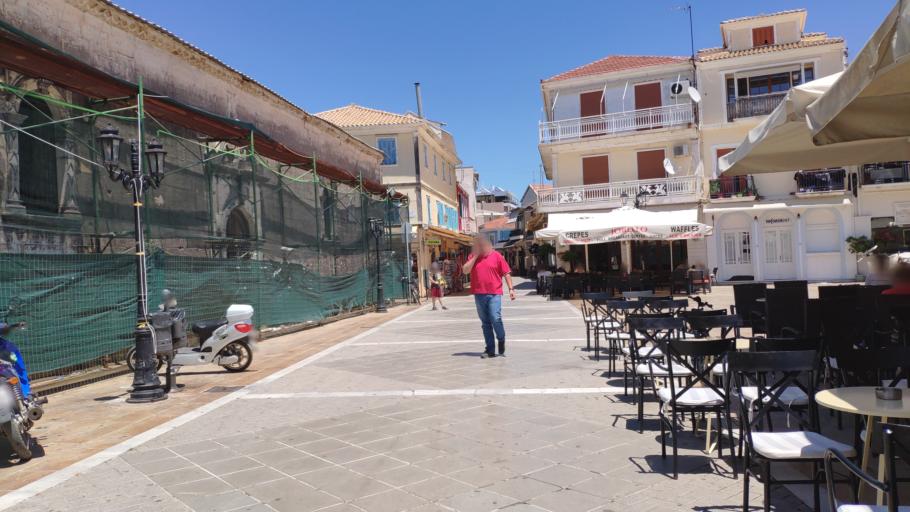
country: GR
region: Ionian Islands
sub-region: Lefkada
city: Lefkada
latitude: 38.8340
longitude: 20.7085
